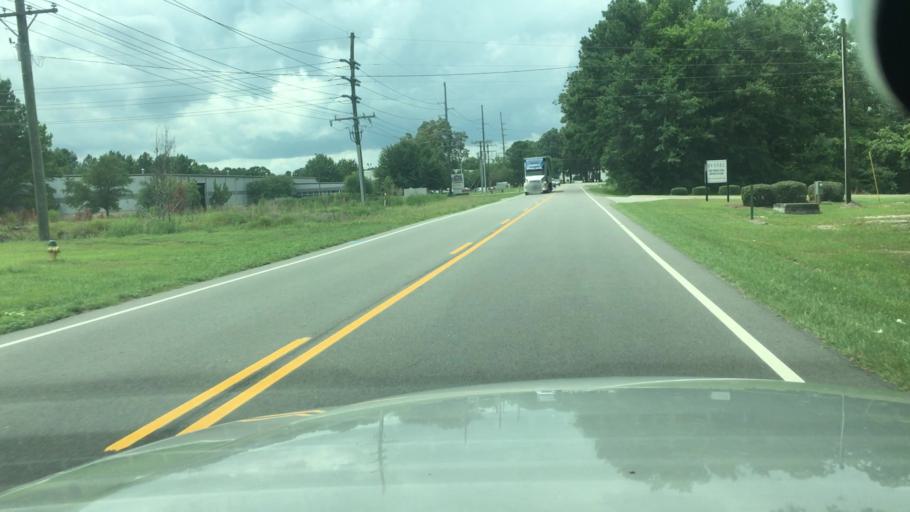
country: US
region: North Carolina
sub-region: Cumberland County
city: Hope Mills
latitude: 34.9509
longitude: -78.8884
